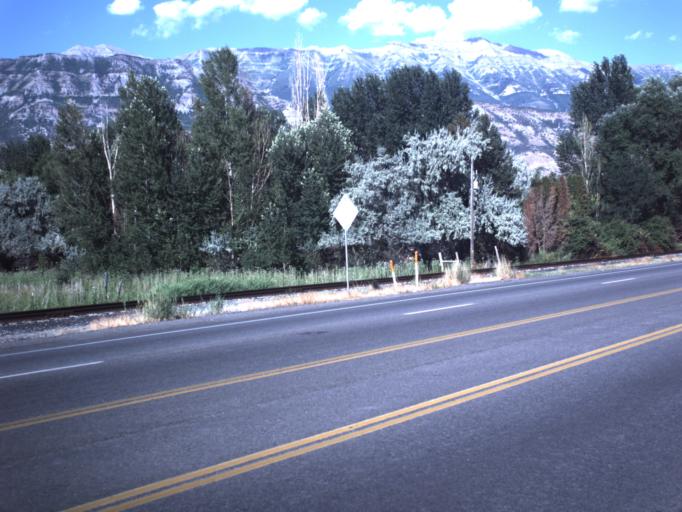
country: US
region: Utah
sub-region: Utah County
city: Pleasant Grove
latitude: 40.3678
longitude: -111.7590
